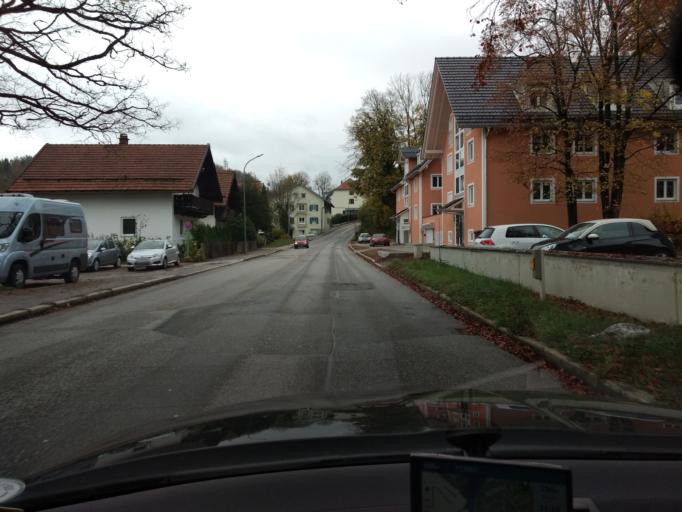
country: DE
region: Bavaria
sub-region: Upper Bavaria
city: Bad Toelz
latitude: 47.7632
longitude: 11.5457
